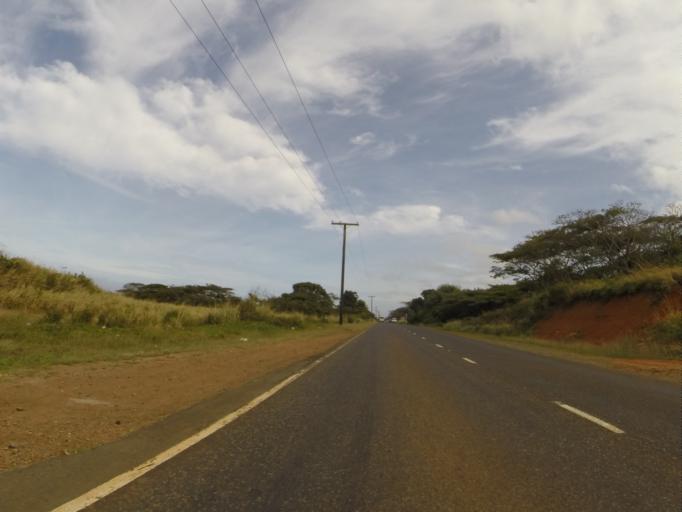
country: FJ
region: Western
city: Nadi
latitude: -18.1611
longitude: 177.4559
